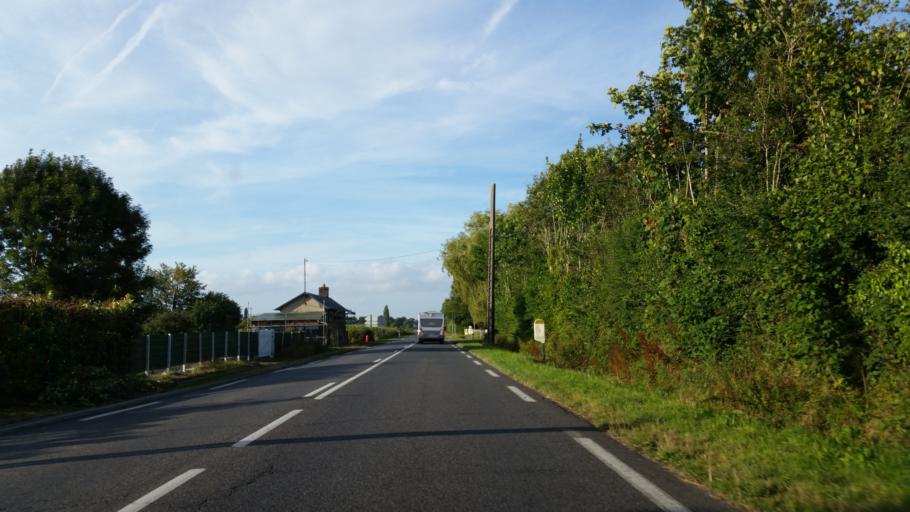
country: FR
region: Lower Normandy
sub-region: Departement du Calvados
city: Saint-Gatien-des-Bois
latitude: 49.3630
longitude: 0.2006
